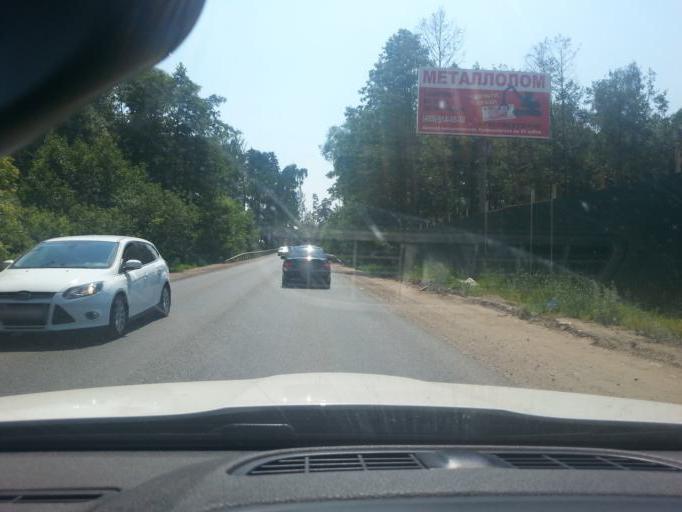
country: RU
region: Moskovskaya
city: Zheleznodorozhnyy
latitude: 55.7173
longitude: 37.9722
